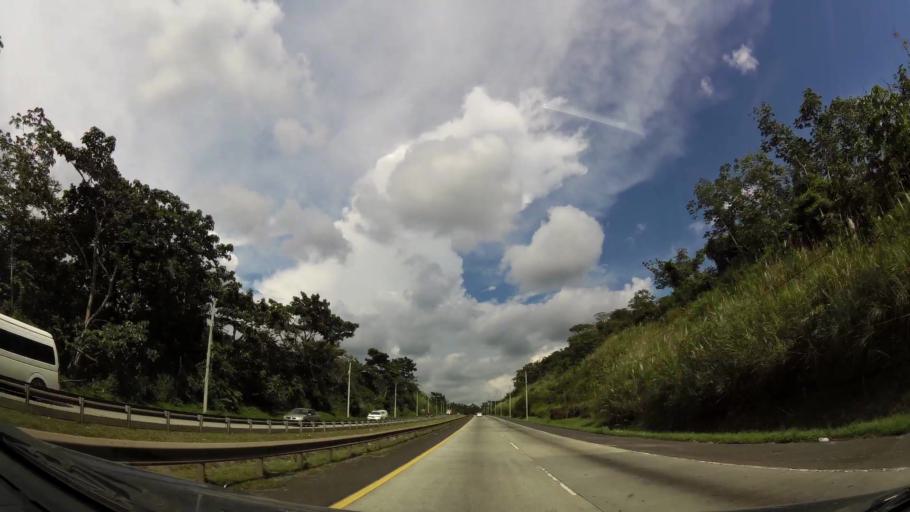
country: PA
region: Panama
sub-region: Distrito de Panama
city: Paraiso
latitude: 9.0368
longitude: -79.5752
